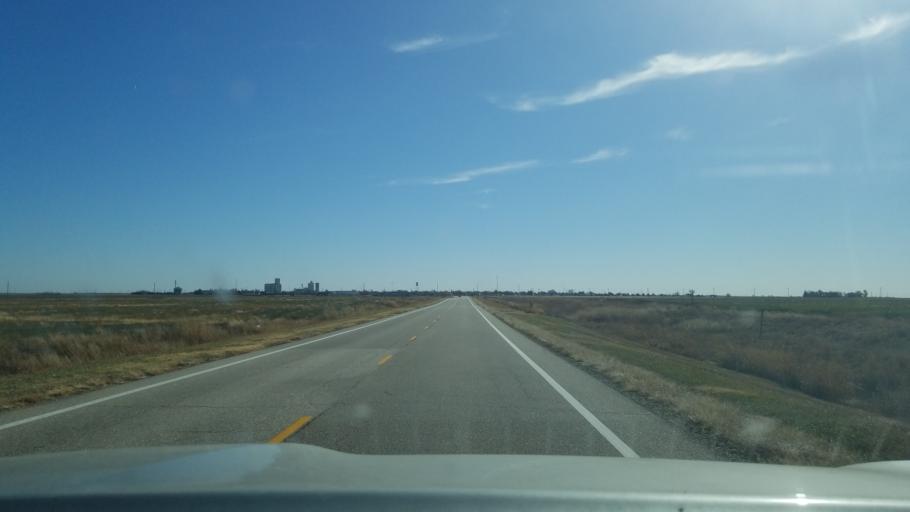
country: US
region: Kansas
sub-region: Kiowa County
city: Greensburg
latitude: 37.5626
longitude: -99.6532
